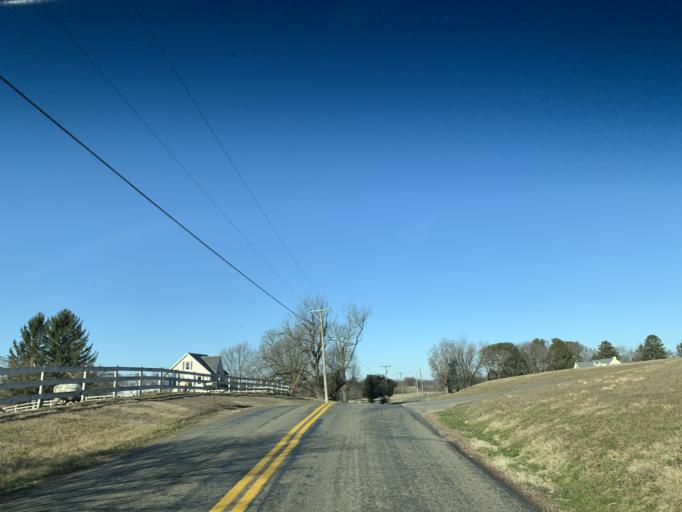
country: US
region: Maryland
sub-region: Harford County
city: Aberdeen
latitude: 39.5855
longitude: -76.2073
